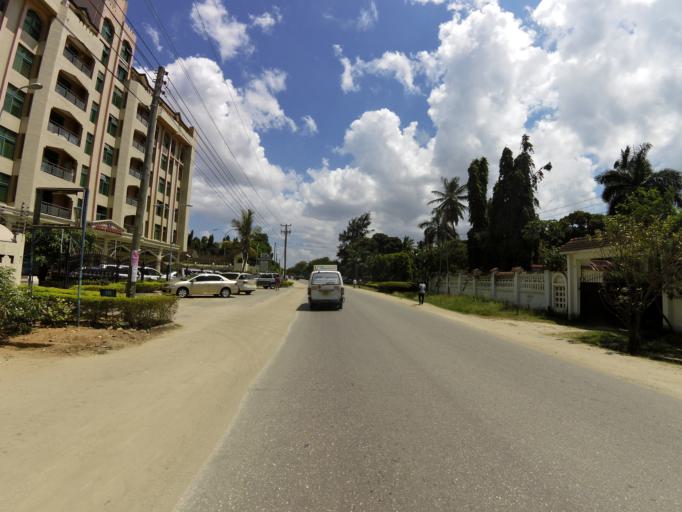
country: TZ
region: Dar es Salaam
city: Magomeni
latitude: -6.7619
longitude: 39.2509
